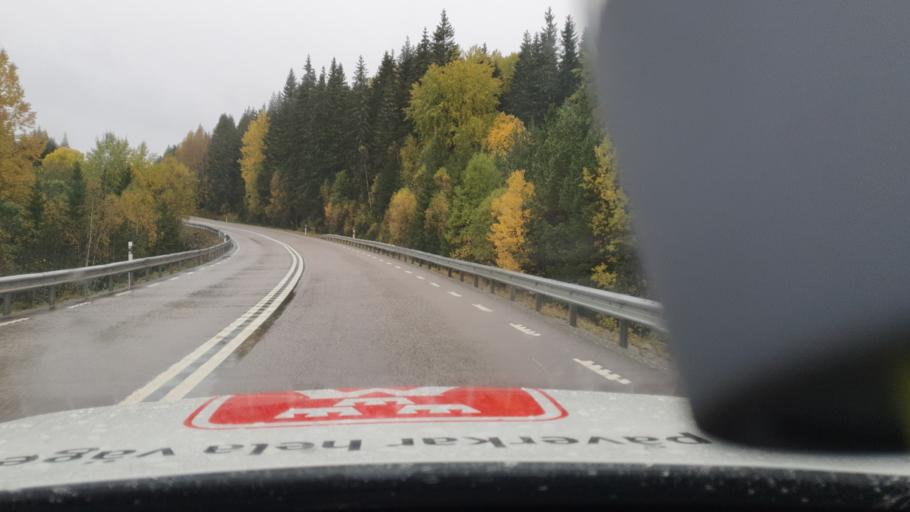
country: SE
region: Vaestra Goetaland
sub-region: Dals-Ed Kommun
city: Ed
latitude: 58.9343
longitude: 12.0458
